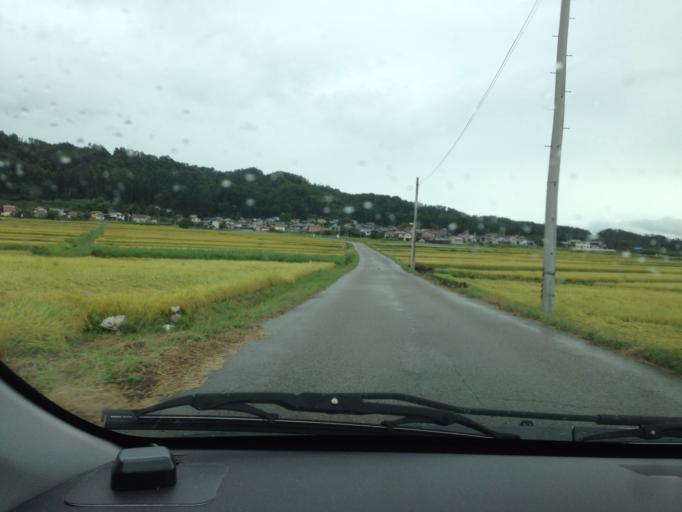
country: JP
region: Fukushima
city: Kitakata
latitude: 37.4839
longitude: 139.8227
